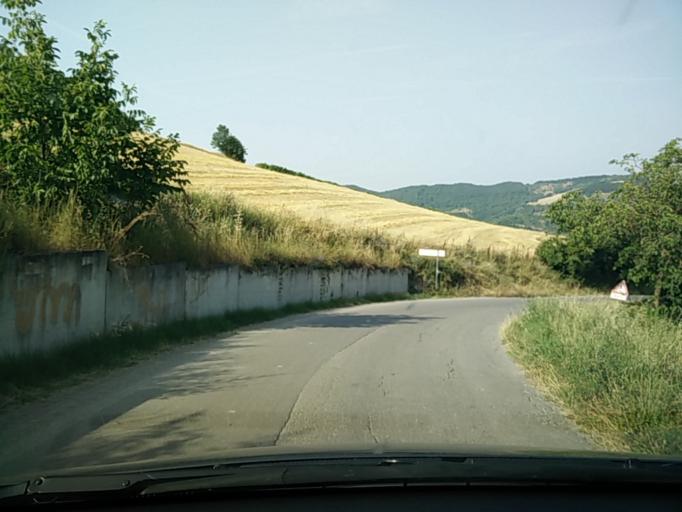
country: IT
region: Lombardy
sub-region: Provincia di Pavia
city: Susella
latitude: 44.9301
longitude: 9.1099
